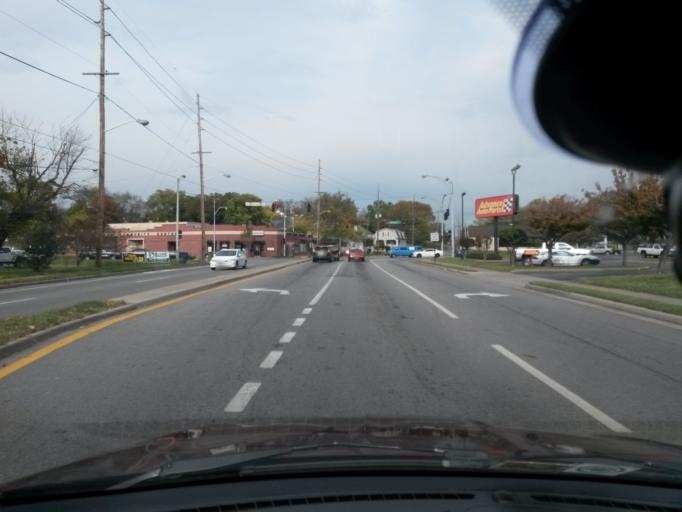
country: US
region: Virginia
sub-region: City of Roanoke
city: Cedar Bluff
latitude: 37.2703
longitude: -79.9212
